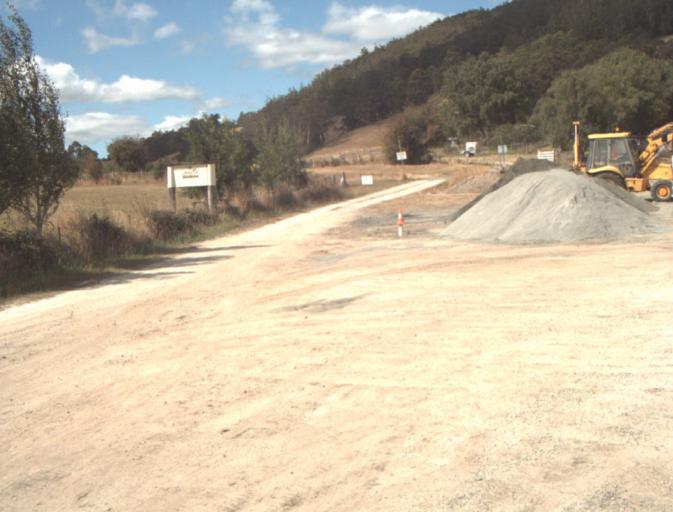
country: AU
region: Tasmania
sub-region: Launceston
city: Mayfield
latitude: -41.2599
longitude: 147.2073
